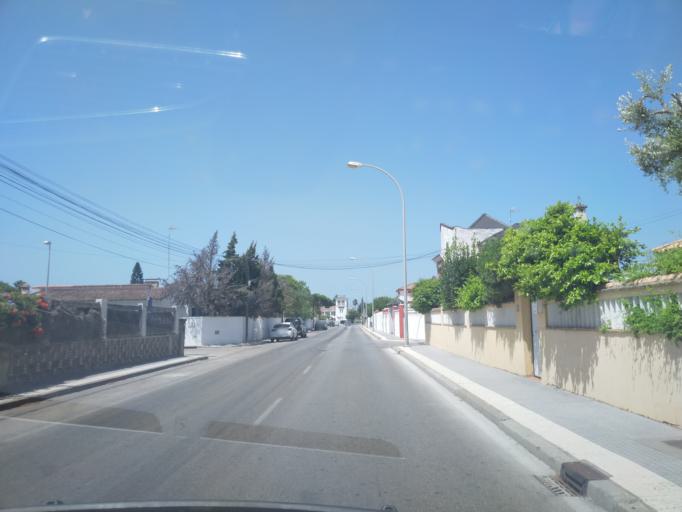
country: ES
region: Andalusia
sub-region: Provincia de Cadiz
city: Chiclana de la Frontera
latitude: 36.3960
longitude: -6.1703
